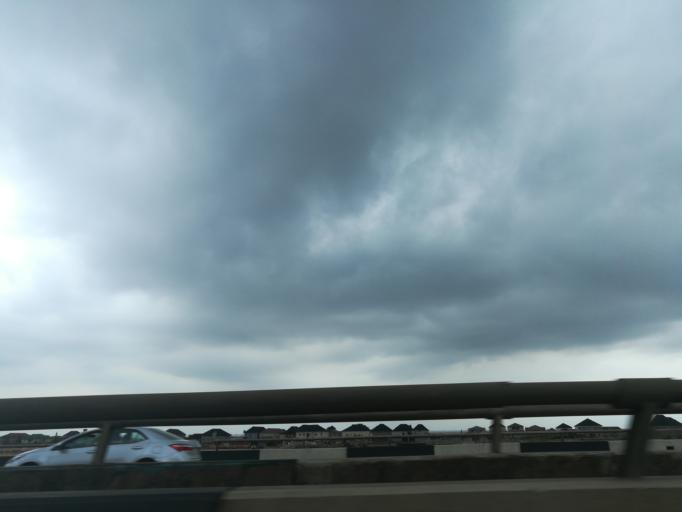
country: NG
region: Lagos
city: Somolu
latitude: 6.5355
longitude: 3.4006
